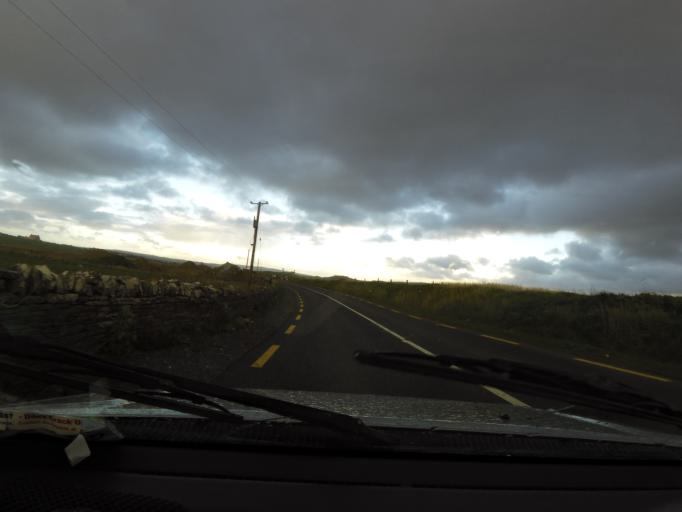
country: IE
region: Munster
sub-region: An Clar
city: Kilrush
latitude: 52.9440
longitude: -9.3722
